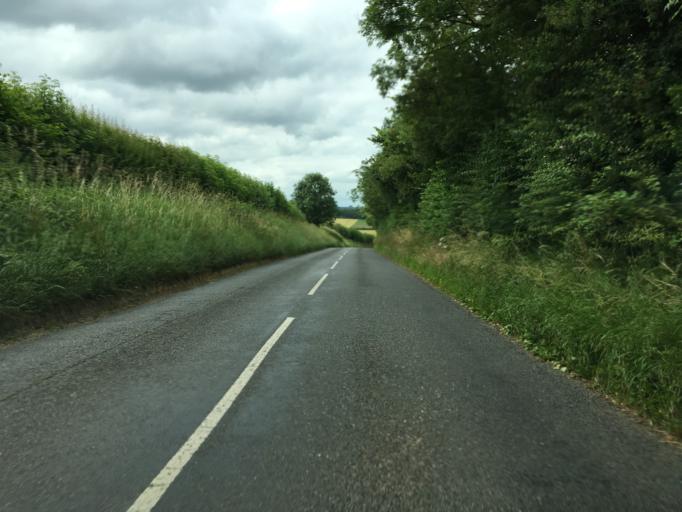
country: GB
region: England
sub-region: Oxfordshire
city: Shipton under Wychwood
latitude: 51.9074
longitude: -1.5980
